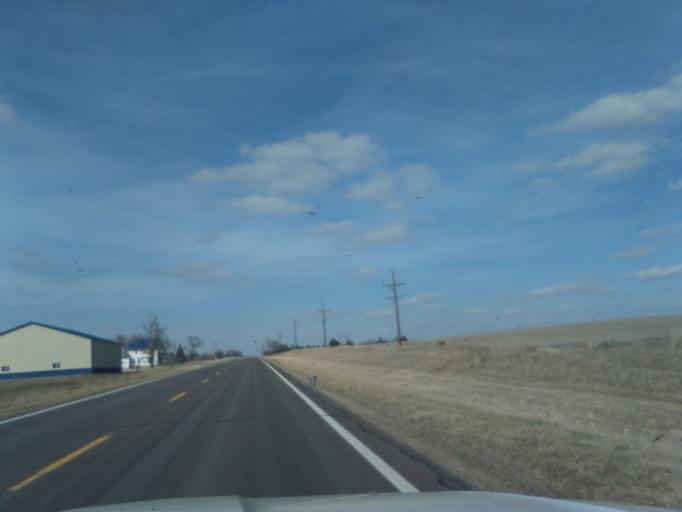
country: US
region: Nebraska
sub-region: Gage County
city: Beatrice
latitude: 40.1273
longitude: -96.9354
